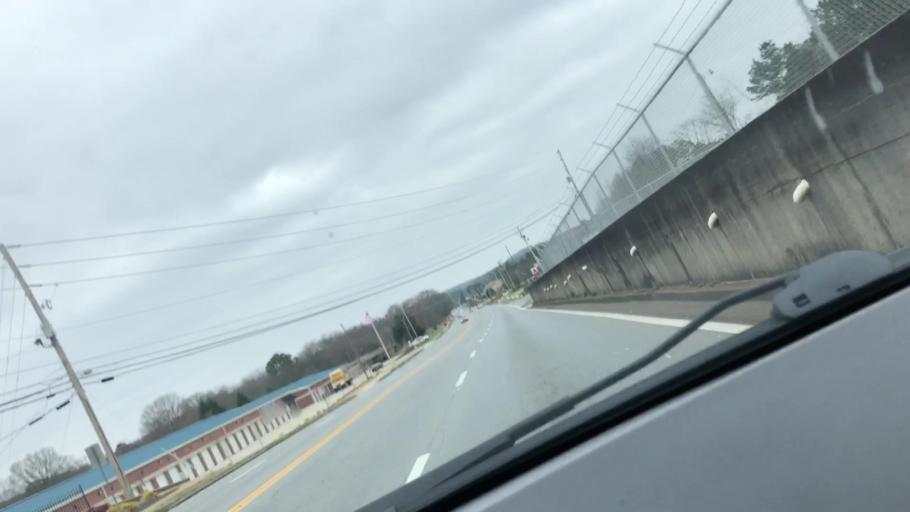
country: US
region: Georgia
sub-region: Bartow County
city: Cartersville
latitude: 34.2094
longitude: -84.8191
